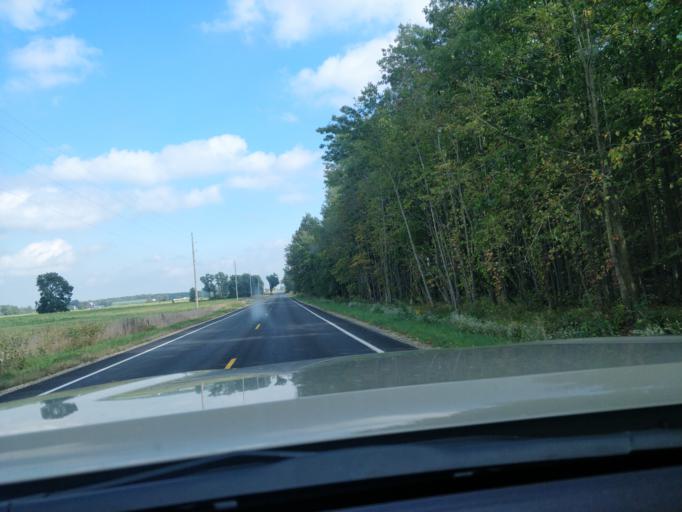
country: US
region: Michigan
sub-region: Ionia County
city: Saranac
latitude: 42.8862
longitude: -85.1313
